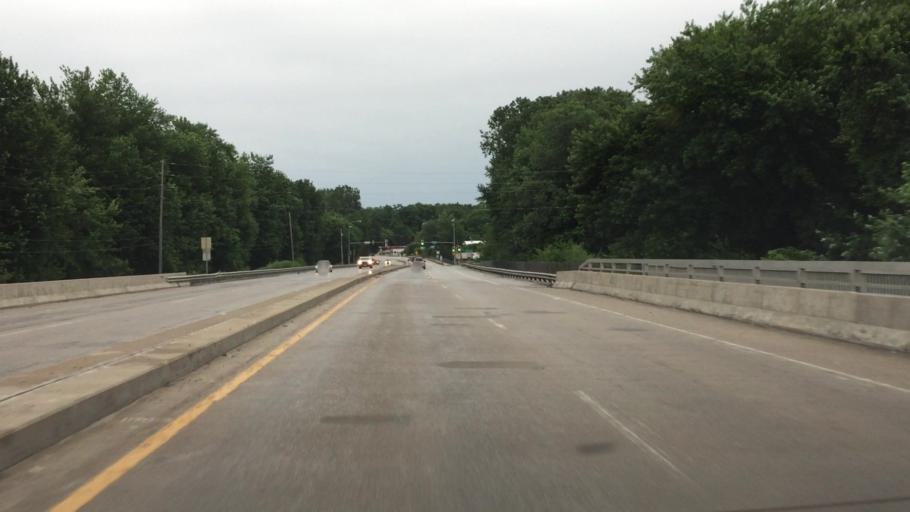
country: US
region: Iowa
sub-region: Lee County
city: Keokuk
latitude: 40.3894
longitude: -91.3622
